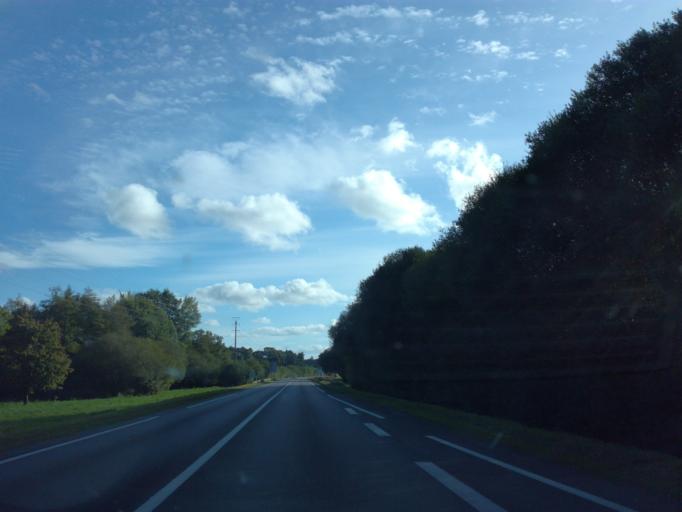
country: FR
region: Brittany
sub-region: Departement du Morbihan
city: Saint-Thuriau
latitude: 48.0520
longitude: -2.9445
